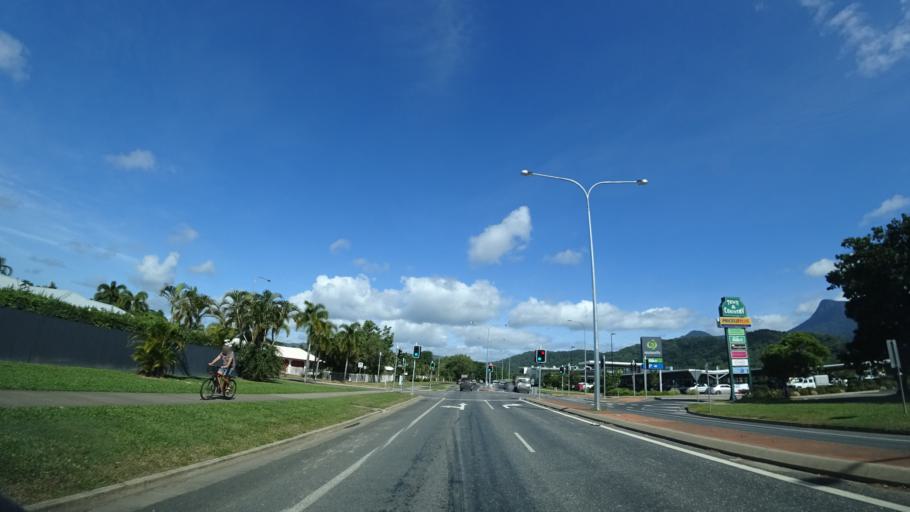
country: AU
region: Queensland
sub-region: Cairns
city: Port Douglas
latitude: -16.4654
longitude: 145.3732
